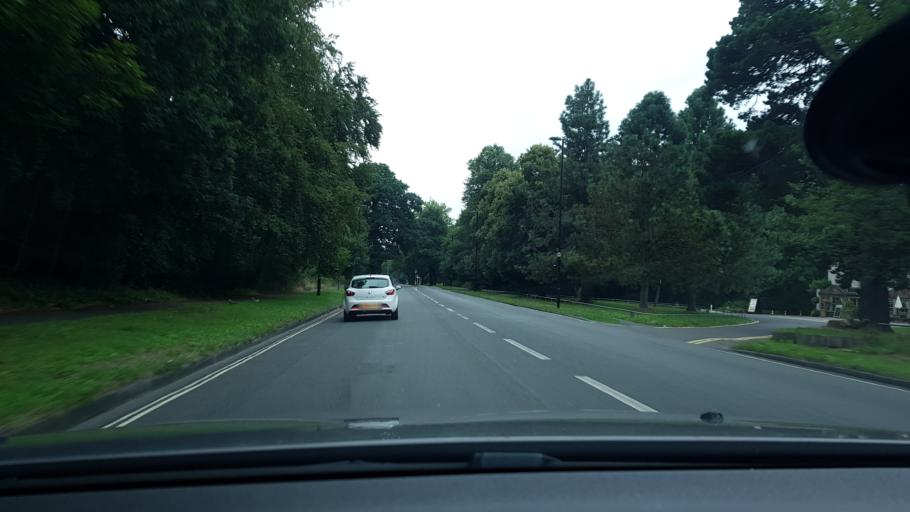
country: GB
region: England
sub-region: Southampton
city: Southampton
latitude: 50.9247
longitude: -1.4053
